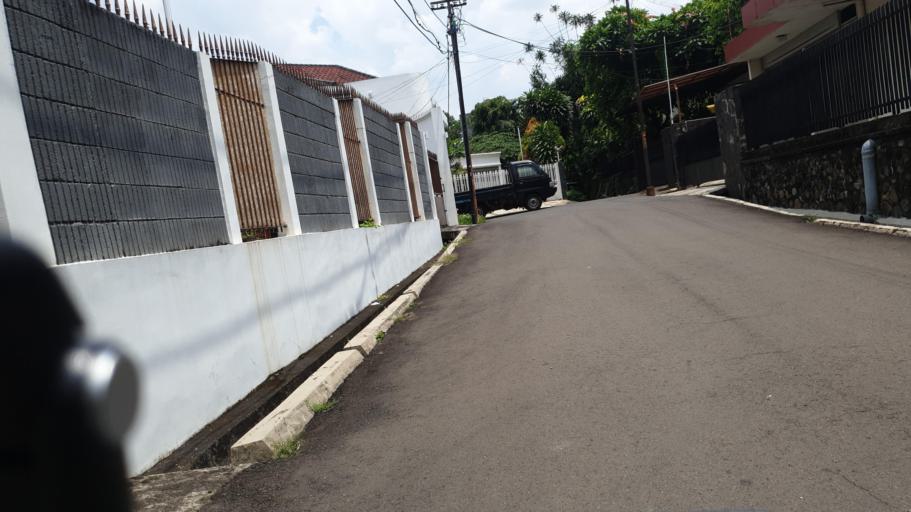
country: ID
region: Banten
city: South Tangerang
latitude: -6.2847
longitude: 106.7923
